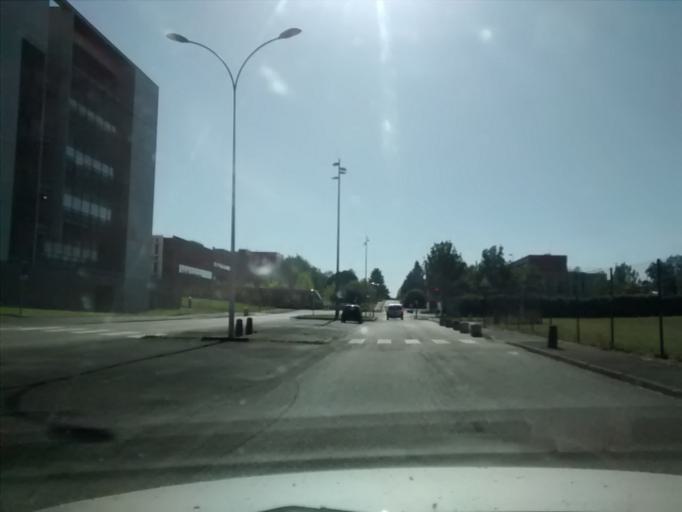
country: FR
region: Pays de la Loire
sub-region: Departement de la Sarthe
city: La Chapelle-Saint-Aubin
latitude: 48.0168
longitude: 0.1629
